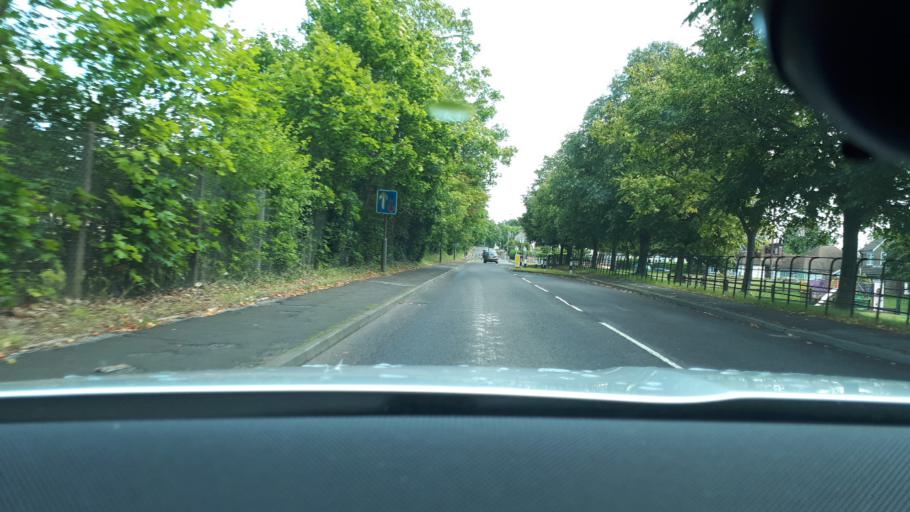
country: GB
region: England
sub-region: Kent
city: Swanley
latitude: 51.4122
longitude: 0.1824
